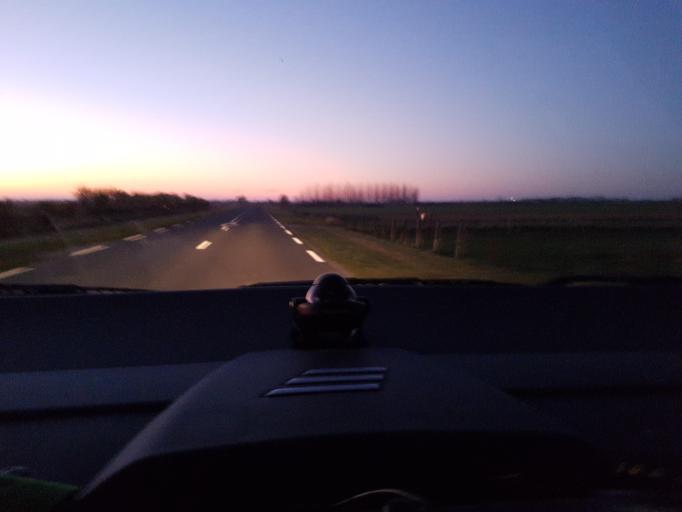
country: FR
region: Picardie
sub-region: Departement de la Somme
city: Pende
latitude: 50.1870
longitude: 1.5756
